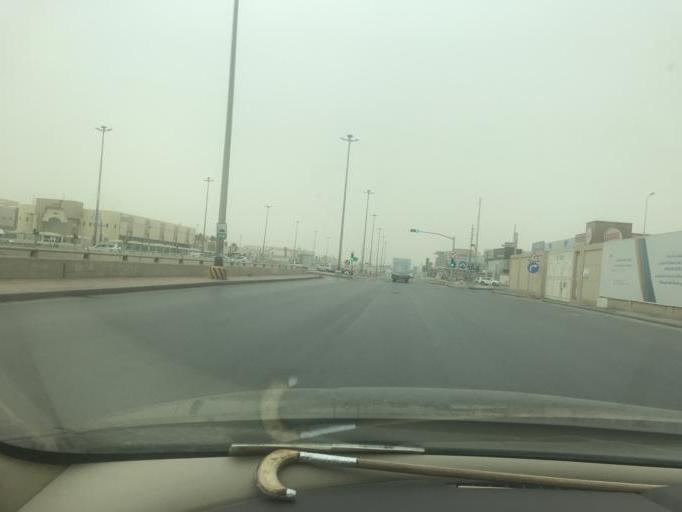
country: SA
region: Ar Riyad
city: Riyadh
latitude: 24.7295
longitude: 46.7863
